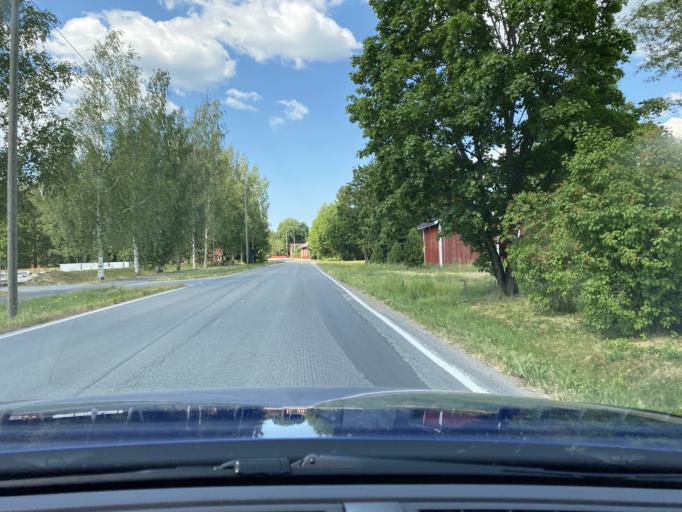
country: FI
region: Satakunta
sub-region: Rauma
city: Eura
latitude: 61.1396
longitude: 22.1235
